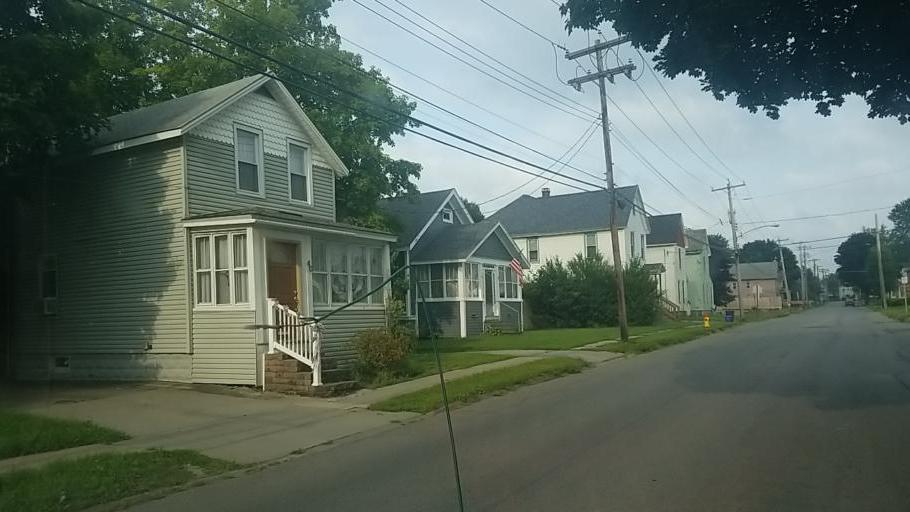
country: US
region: New York
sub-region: Fulton County
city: Johnstown
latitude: 43.0144
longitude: -74.3662
